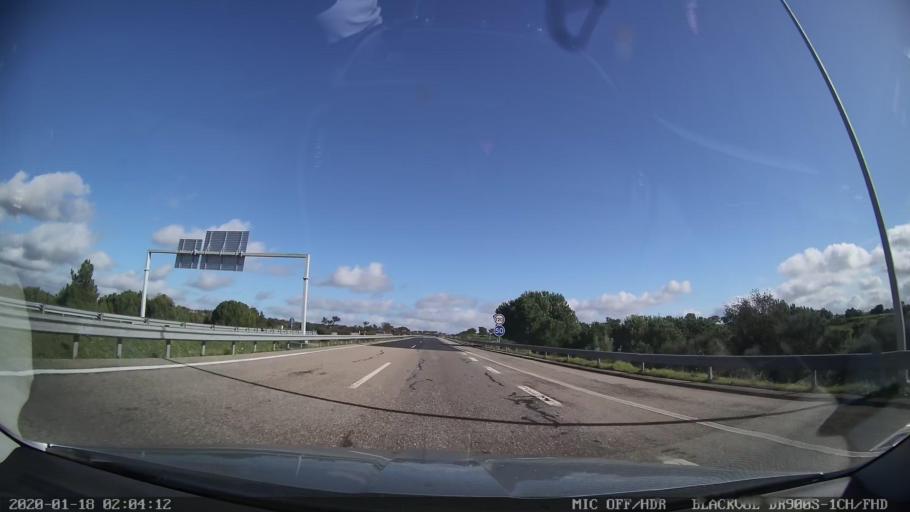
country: PT
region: Evora
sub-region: Vendas Novas
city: Vendas Novas
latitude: 38.6470
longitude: -8.4280
